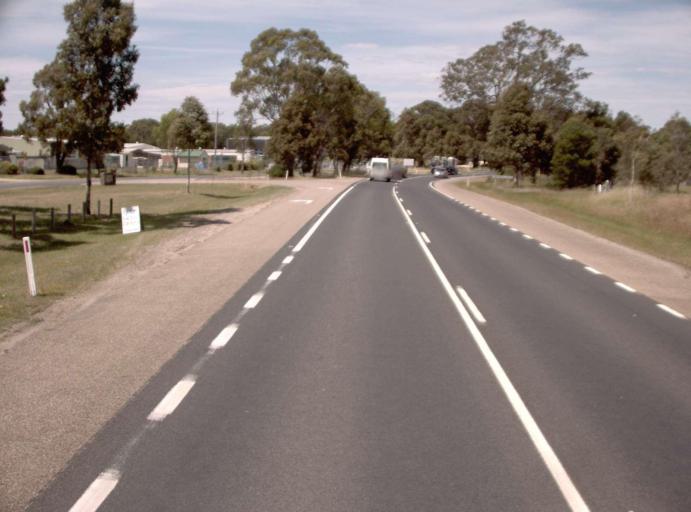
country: AU
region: Victoria
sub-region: Wellington
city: Sale
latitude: -37.9629
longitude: 147.0883
